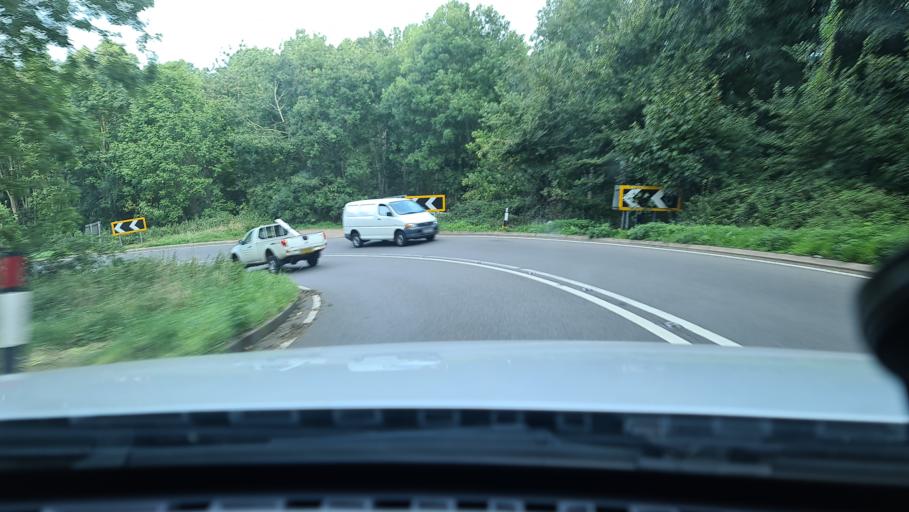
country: GB
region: England
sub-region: Oxfordshire
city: Hanwell
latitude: 52.1117
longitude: -1.4764
